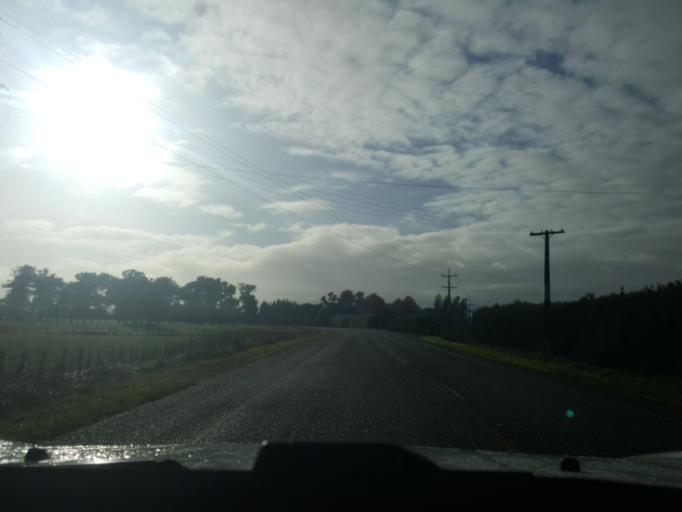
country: NZ
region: Waikato
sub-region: Waipa District
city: Cambridge
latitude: -37.7796
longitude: 175.3984
